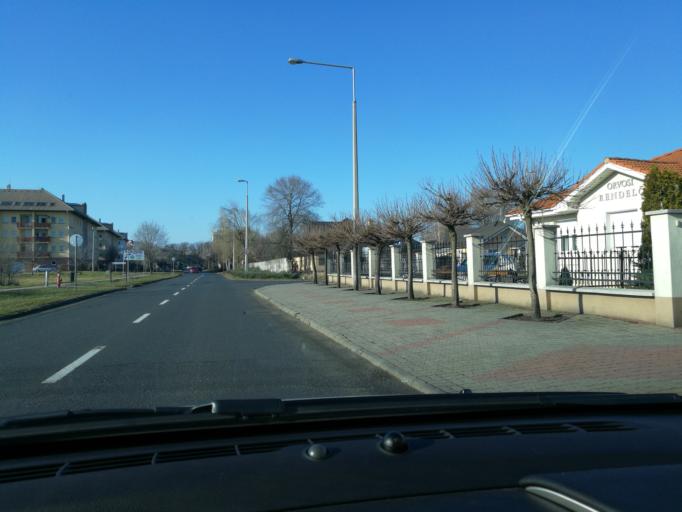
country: HU
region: Szabolcs-Szatmar-Bereg
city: Nyiregyhaza
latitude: 47.9733
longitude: 21.7331
